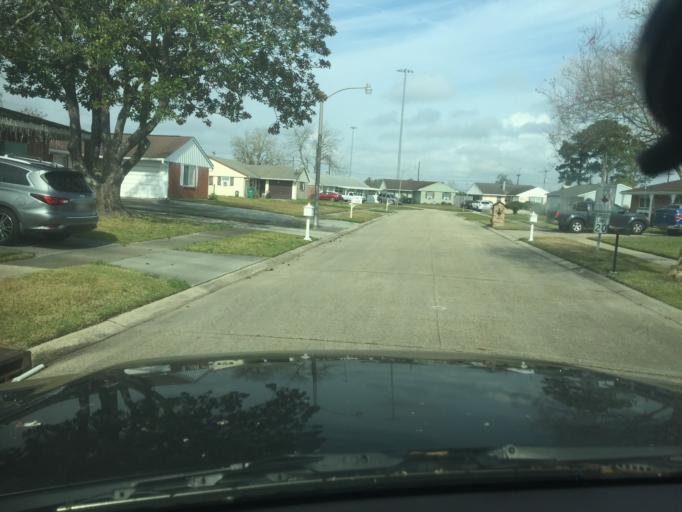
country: US
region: Louisiana
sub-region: Jefferson Parish
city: Avondale
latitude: 29.9154
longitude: -90.2037
